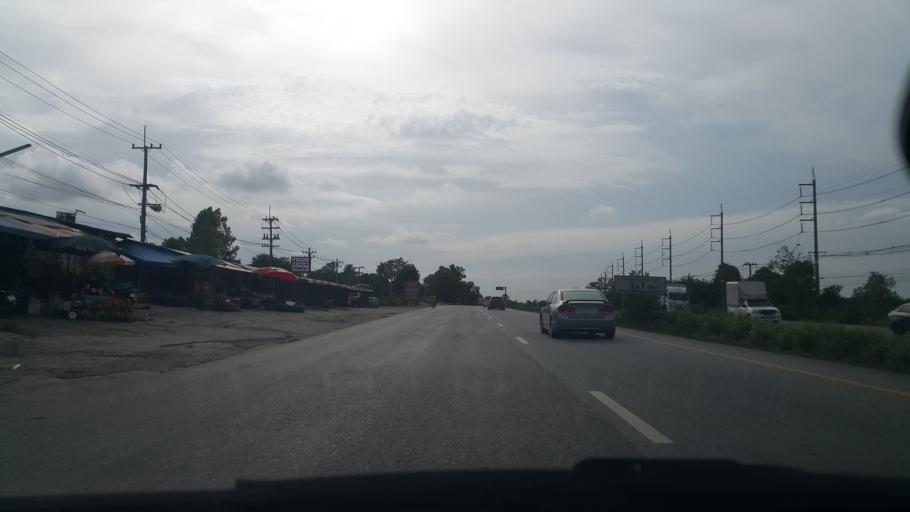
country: TH
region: Rayong
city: Nikhom Phattana
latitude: 12.8683
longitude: 101.0703
